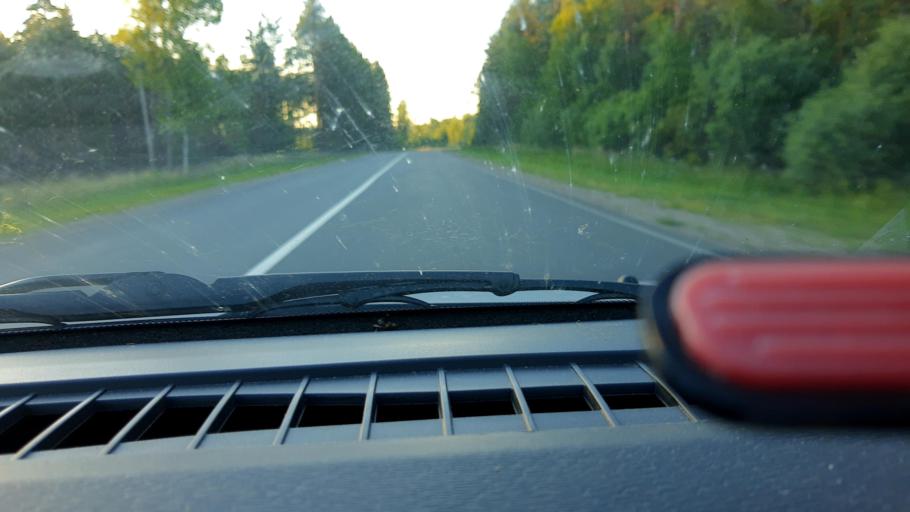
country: RU
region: Nizjnij Novgorod
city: Uren'
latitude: 57.3674
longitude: 45.6945
